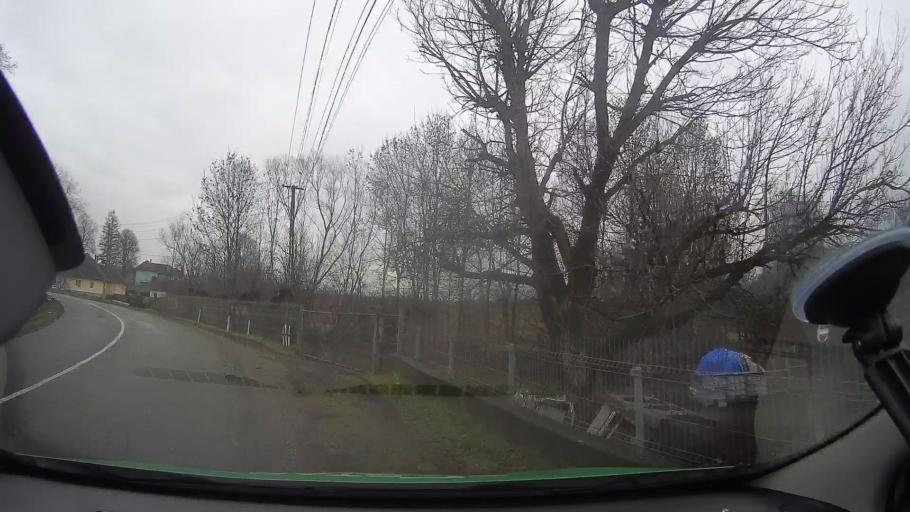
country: RO
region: Arad
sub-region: Comuna Varfurile
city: Varfurile
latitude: 46.3105
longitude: 22.5194
